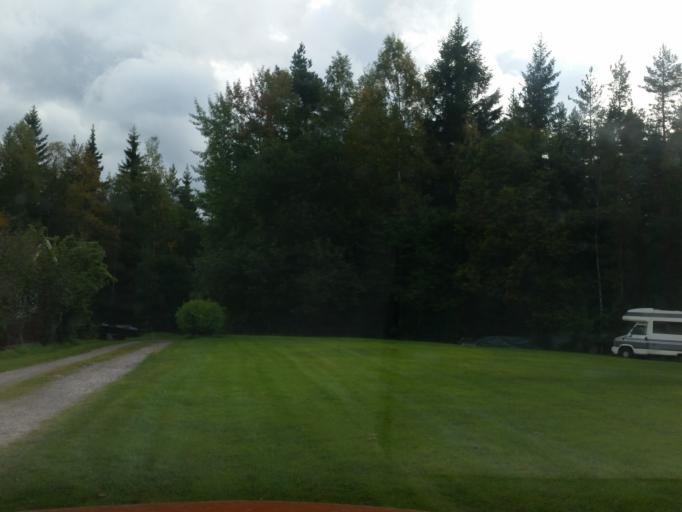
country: SE
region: Dalarna
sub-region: Gagnefs Kommun
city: Gagnef
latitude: 60.6663
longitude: 15.1307
